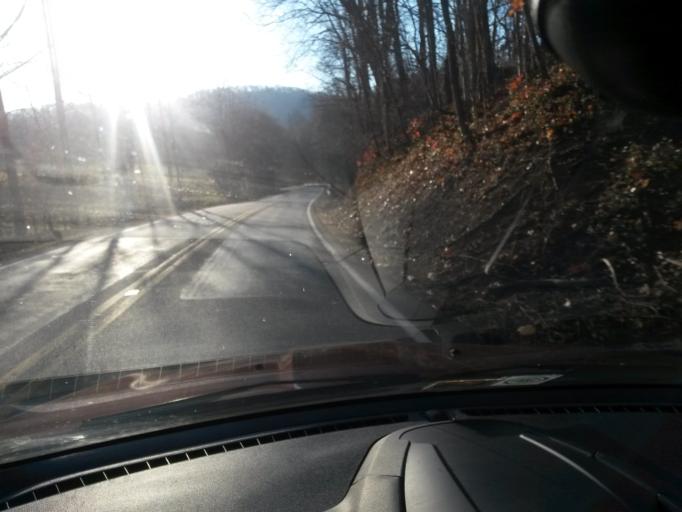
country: US
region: Virginia
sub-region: Amherst County
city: Amherst
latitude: 37.6429
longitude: -79.1221
